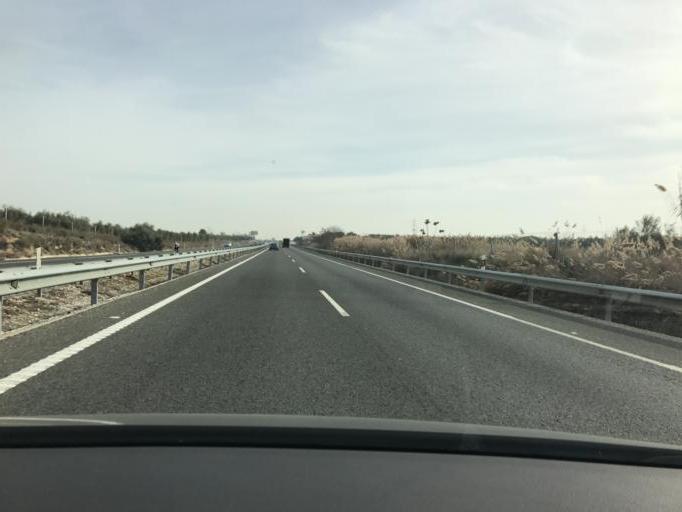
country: ES
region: Andalusia
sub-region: Provincia de Granada
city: Villanueva de Mesia
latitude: 37.1937
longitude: -3.9872
